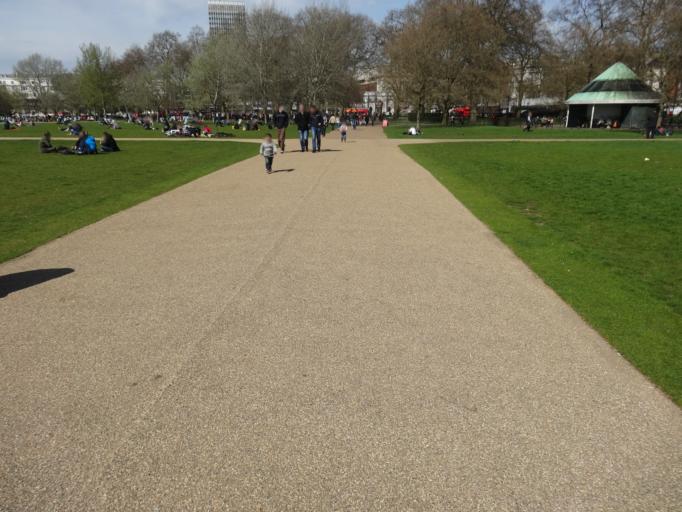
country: GB
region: England
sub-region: Greater London
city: Chelsea
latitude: 51.5105
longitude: -0.1591
